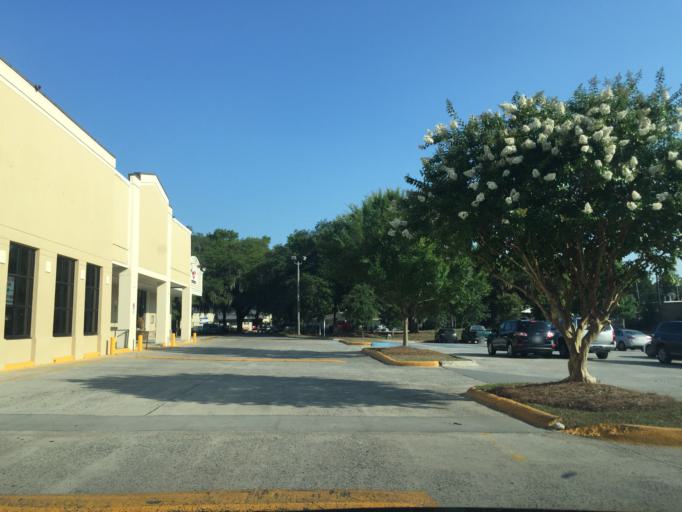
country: US
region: Georgia
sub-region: Chatham County
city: Isle of Hope
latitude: 31.9871
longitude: -81.0738
